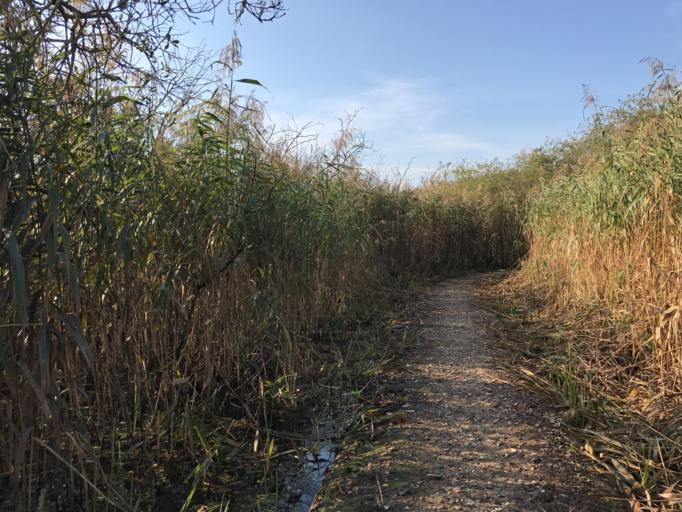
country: DK
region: Central Jutland
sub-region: Silkeborg Kommune
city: Svejbaek
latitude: 56.2009
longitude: 9.6492
